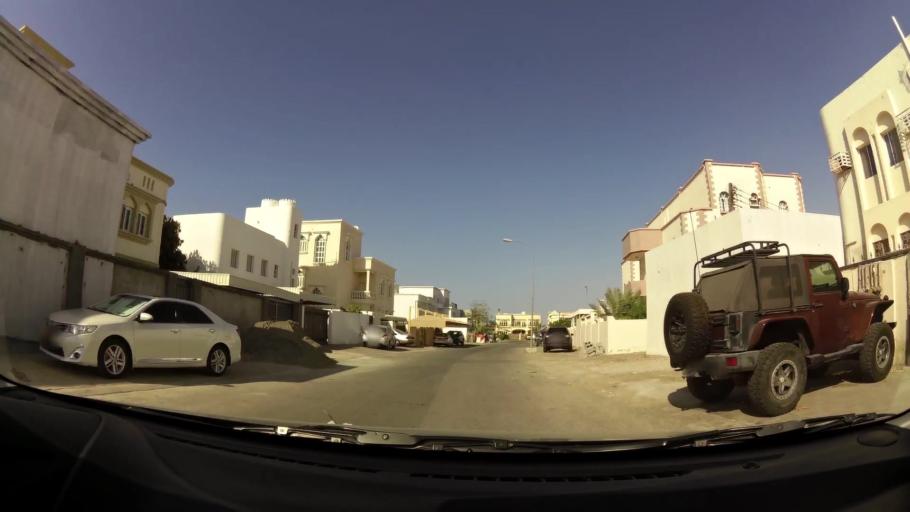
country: OM
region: Muhafazat Masqat
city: As Sib al Jadidah
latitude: 23.6209
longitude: 58.2076
